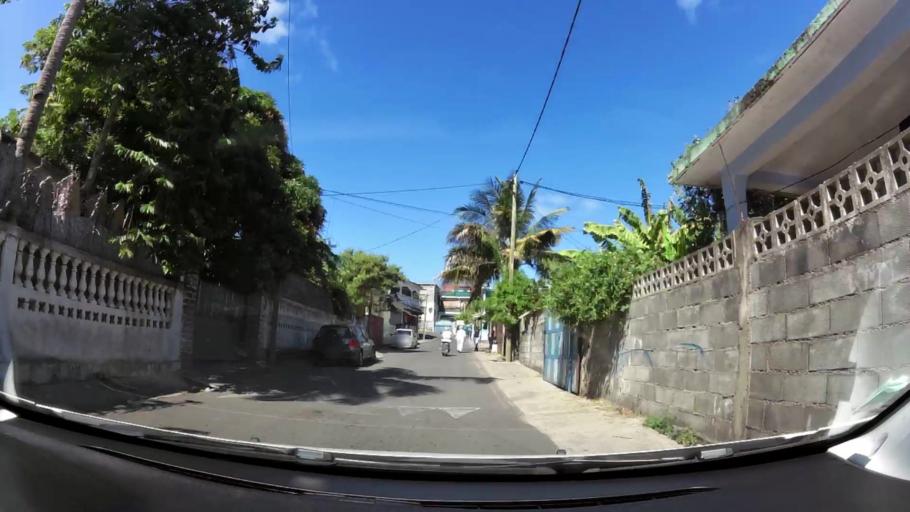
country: YT
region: Pamandzi
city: Pamandzi
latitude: -12.7872
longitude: 45.2783
